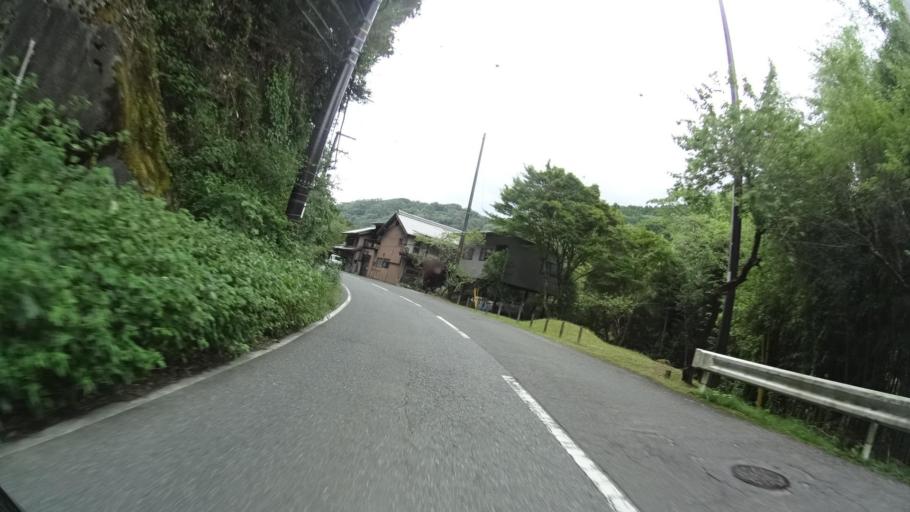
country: JP
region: Mie
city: Nabari
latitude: 34.7055
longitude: 136.0256
